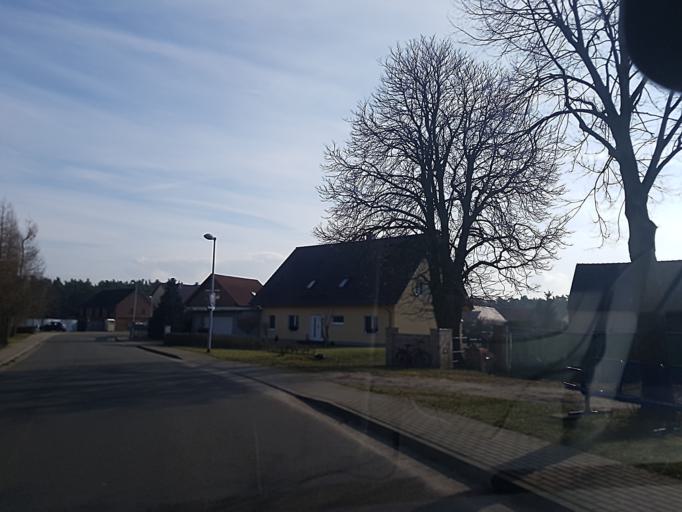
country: DE
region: Brandenburg
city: Wenzlow
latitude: 52.3255
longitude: 12.4407
